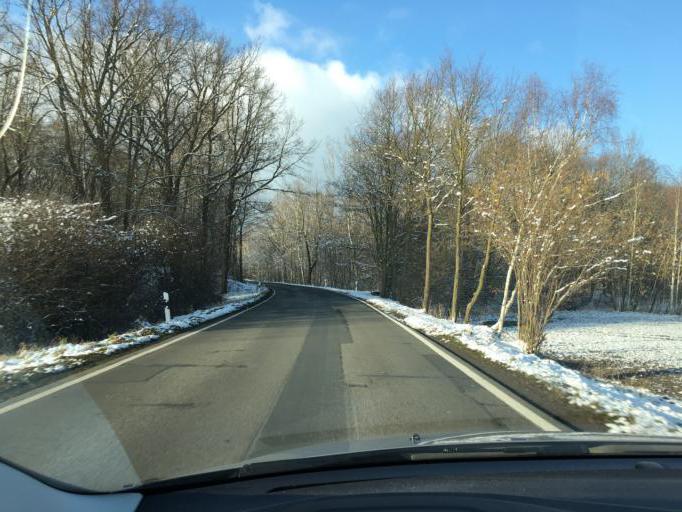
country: DE
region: Saxony
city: Grimma
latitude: 51.2671
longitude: 12.6704
